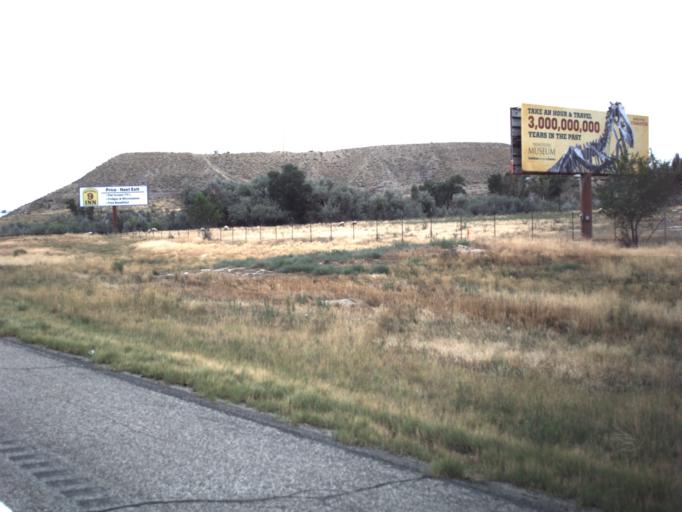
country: US
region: Utah
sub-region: Carbon County
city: Carbonville
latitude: 39.6145
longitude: -110.8392
